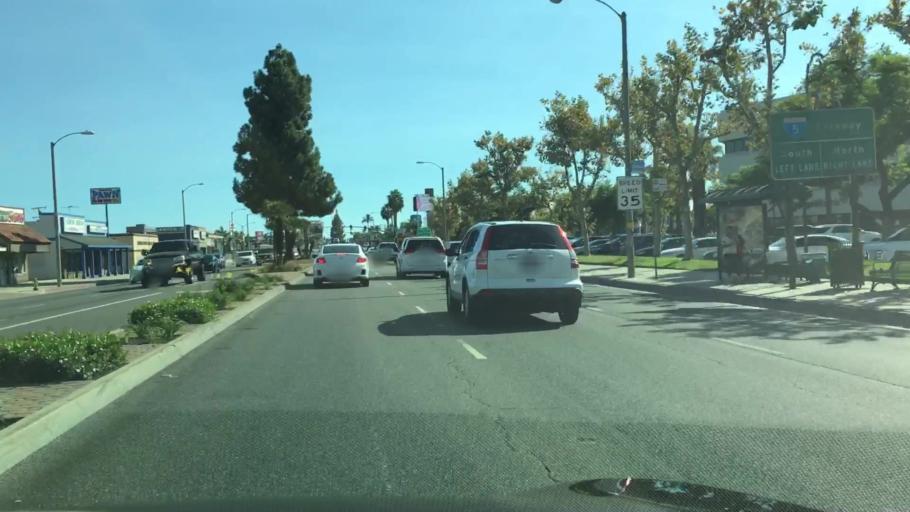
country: US
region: California
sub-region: Orange County
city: Buena Park
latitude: 33.8696
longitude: -117.9983
